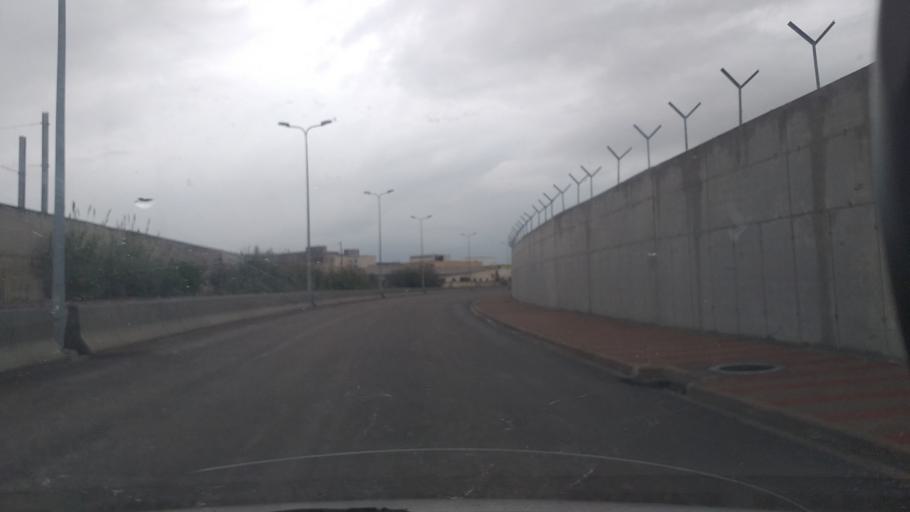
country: TN
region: Ariana
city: Ariana
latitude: 36.8591
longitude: 10.2142
